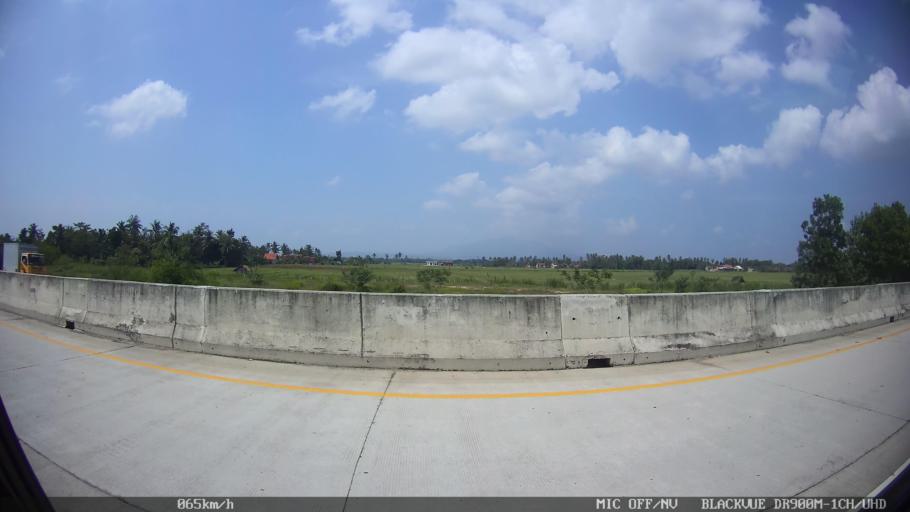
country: ID
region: Lampung
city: Natar
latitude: -5.2927
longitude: 105.2339
